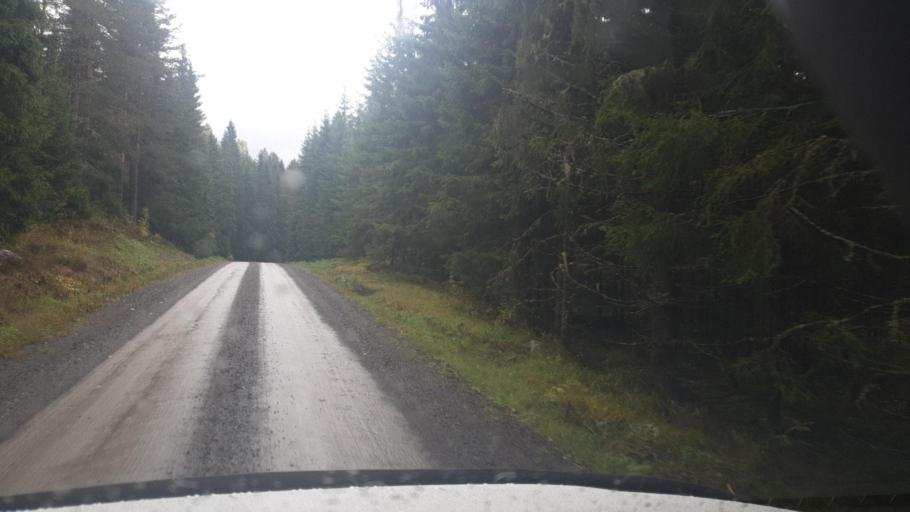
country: SE
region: Vaermland
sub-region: Sunne Kommun
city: Sunne
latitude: 59.8592
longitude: 12.8401
